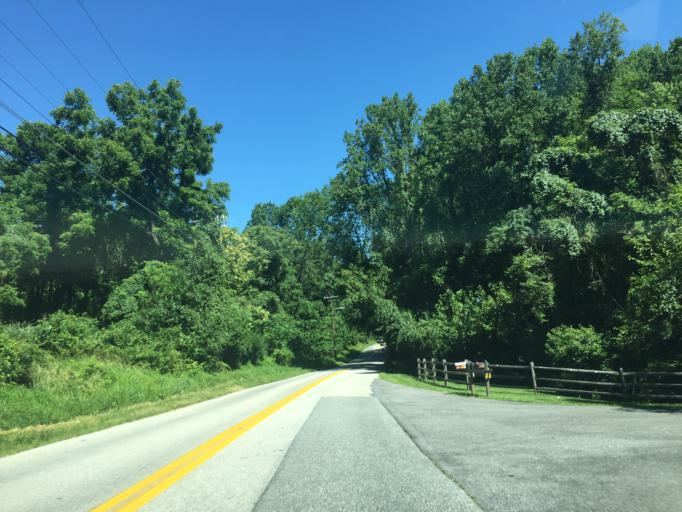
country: US
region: Maryland
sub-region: Baltimore County
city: Timonium
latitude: 39.4627
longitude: -76.6025
